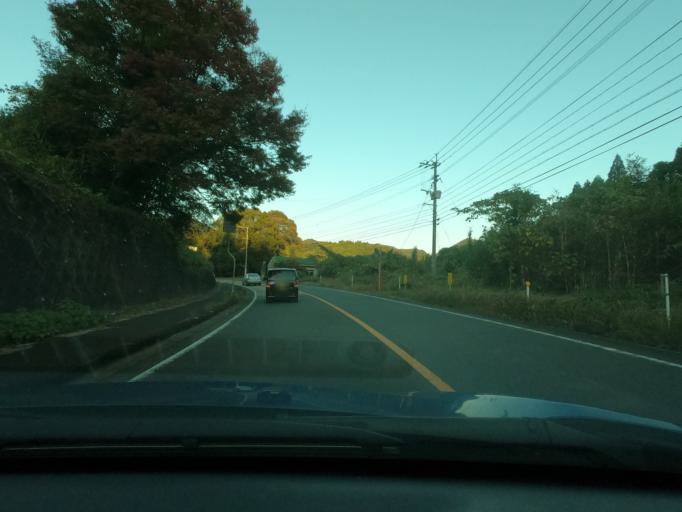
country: JP
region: Kagoshima
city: Satsumasendai
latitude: 31.7964
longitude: 130.4769
